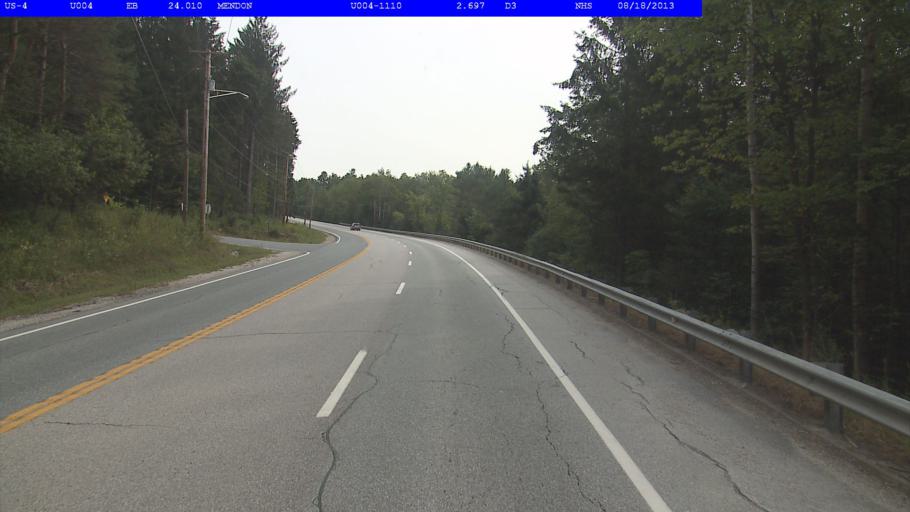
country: US
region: Vermont
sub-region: Rutland County
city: Rutland
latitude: 43.6482
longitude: -72.9002
